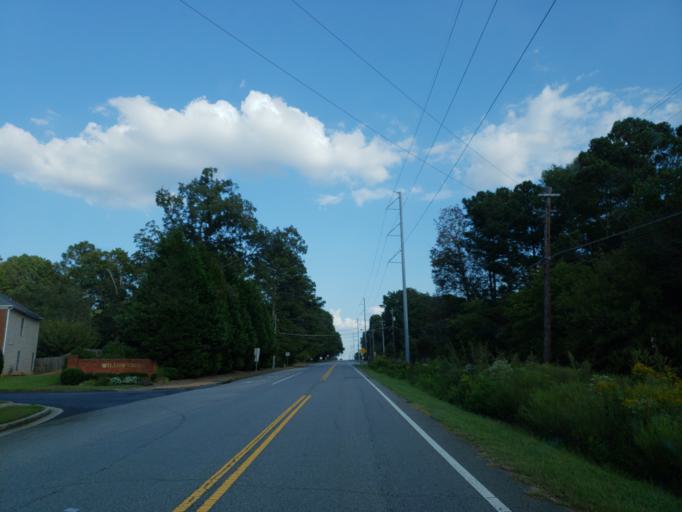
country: US
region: Georgia
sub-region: Fulton County
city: Alpharetta
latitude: 34.0695
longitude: -84.3318
